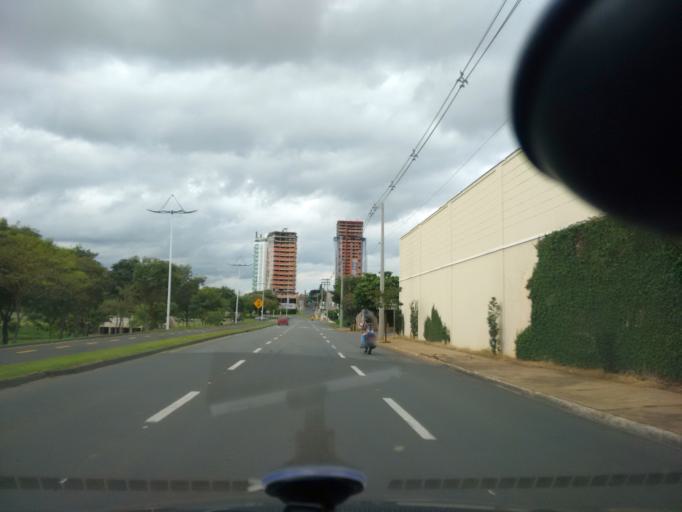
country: BR
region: Sao Paulo
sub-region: Indaiatuba
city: Indaiatuba
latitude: -23.0896
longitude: -47.2242
